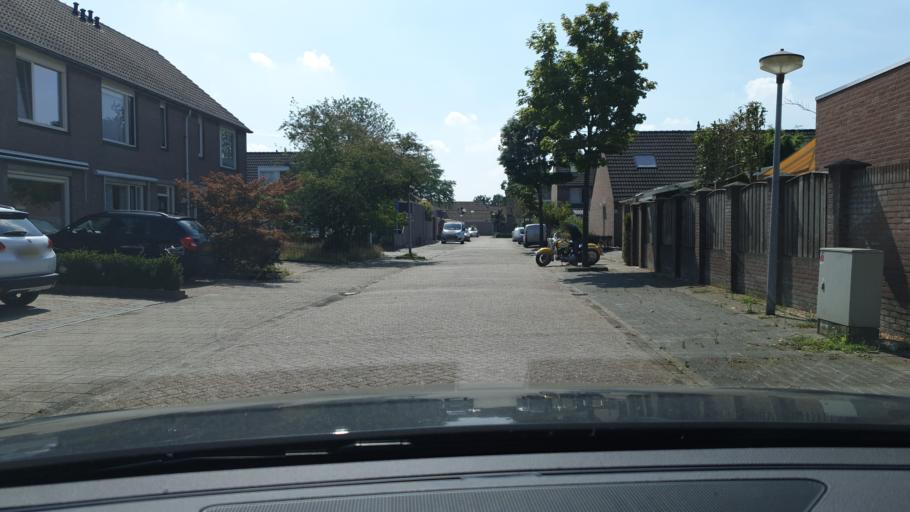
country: NL
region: North Brabant
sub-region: Gemeente Eindhoven
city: Meerhoven
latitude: 51.4831
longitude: 5.4438
